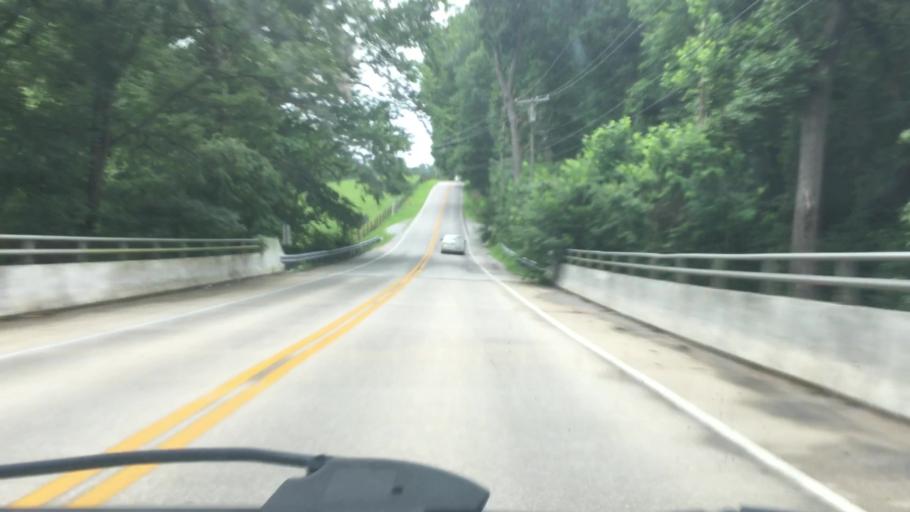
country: US
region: Maryland
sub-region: Howard County
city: North Laurel
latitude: 39.1600
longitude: -76.8520
